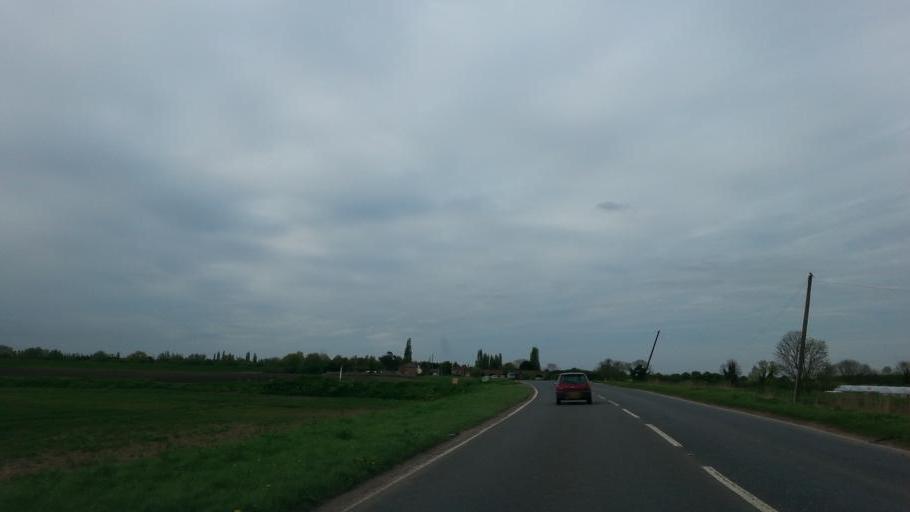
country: GB
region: England
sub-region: Cambridgeshire
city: March
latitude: 52.5982
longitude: 0.0616
